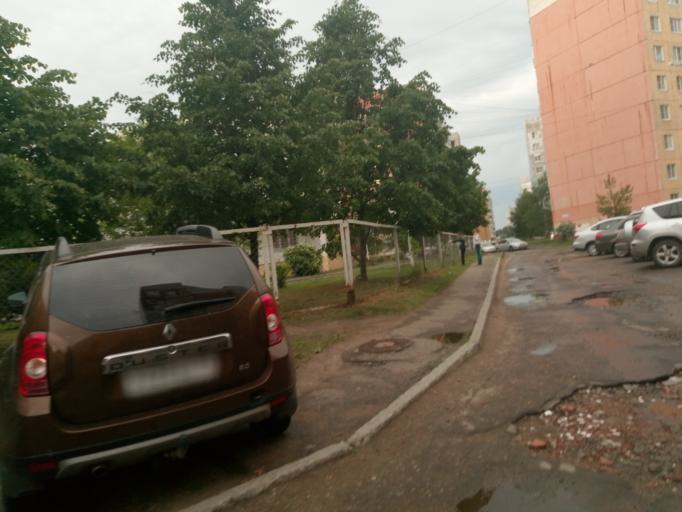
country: RU
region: Jaroslavl
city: Yaroslavl
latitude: 57.6495
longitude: 39.9527
